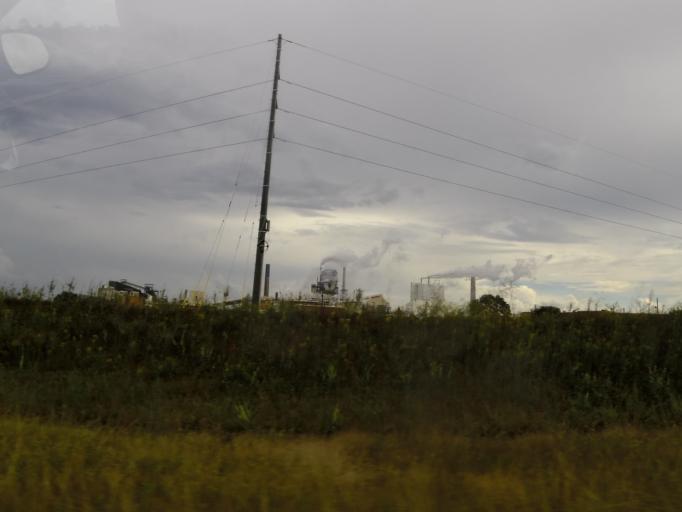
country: US
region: Georgia
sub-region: Wayne County
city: Jesup
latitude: 31.6628
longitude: -81.8466
